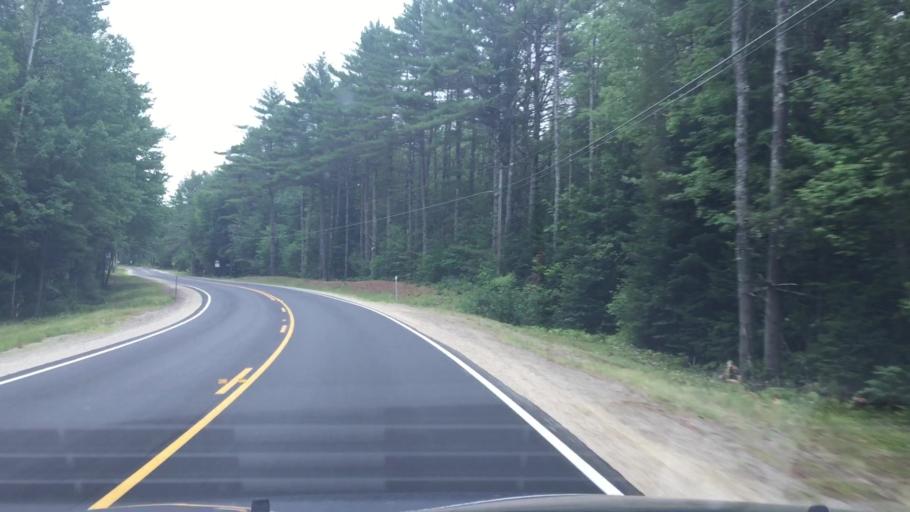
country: US
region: New Hampshire
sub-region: Carroll County
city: Freedom
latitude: 43.8288
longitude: -71.0762
